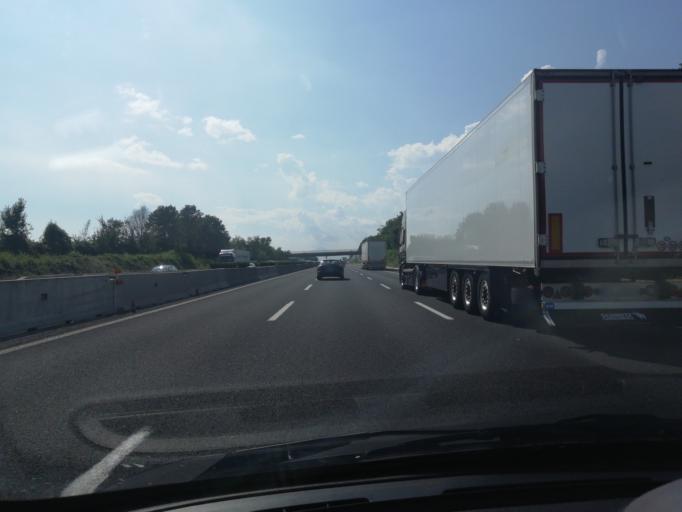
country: IT
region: Latium
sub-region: Provincia di Frosinone
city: Pofi
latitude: 41.5523
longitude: 13.4450
